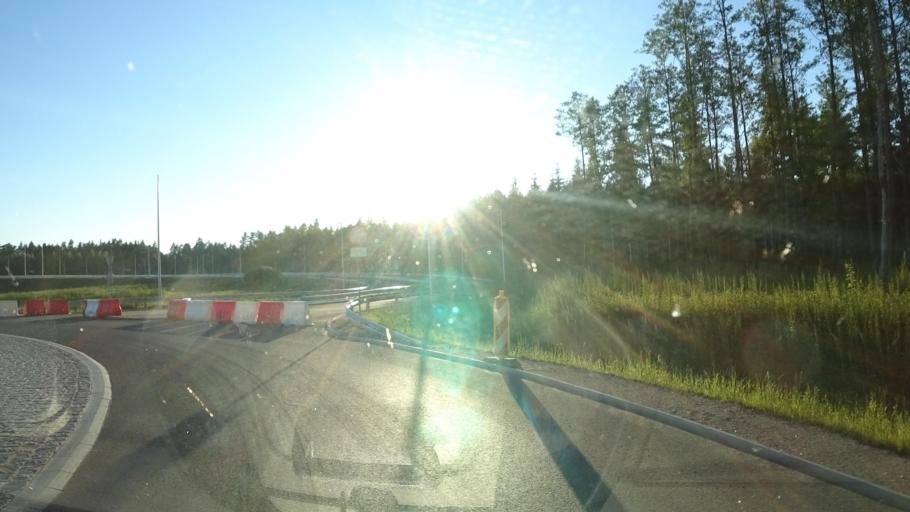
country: PL
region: Warmian-Masurian Voivodeship
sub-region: Powiat elcki
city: Elk
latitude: 53.8405
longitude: 22.4184
